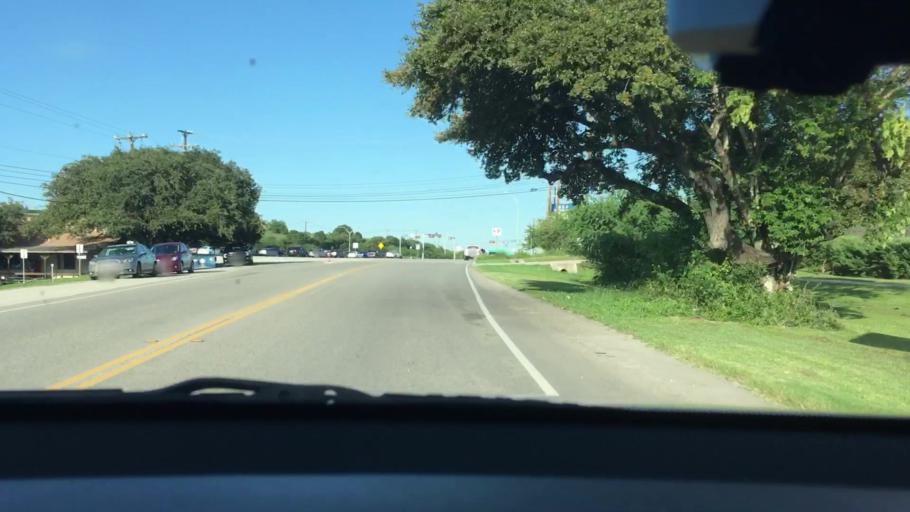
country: US
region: Texas
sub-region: Bexar County
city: Live Oak
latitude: 29.5506
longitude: -98.3571
